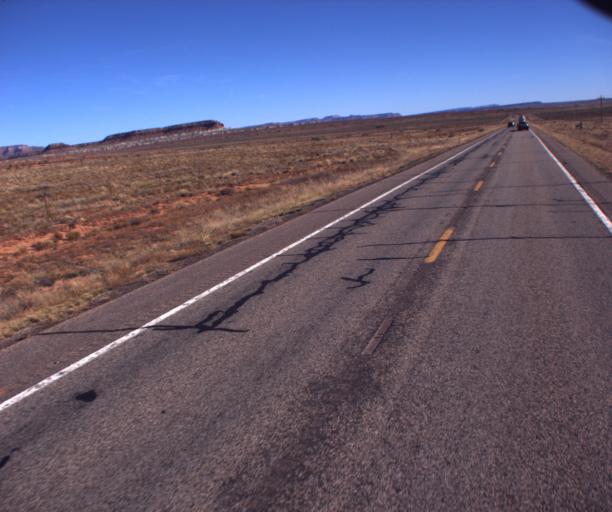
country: US
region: Arizona
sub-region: Coconino County
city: Fredonia
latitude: 36.8903
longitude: -112.6214
